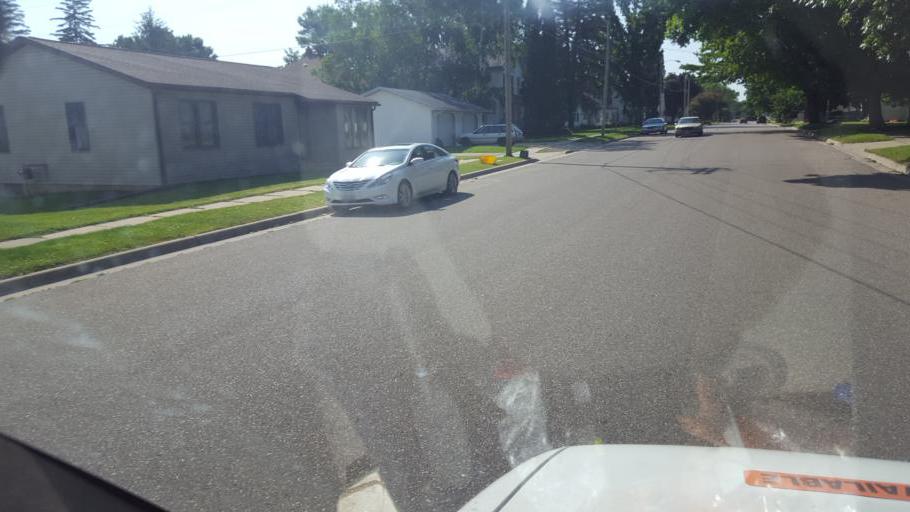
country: US
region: Wisconsin
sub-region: Vernon County
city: Hillsboro
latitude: 43.6528
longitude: -90.3428
